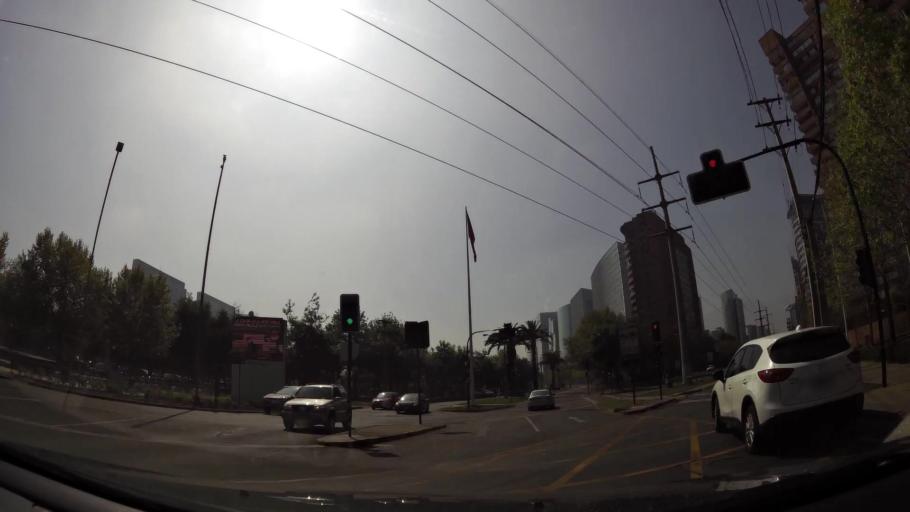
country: CL
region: Santiago Metropolitan
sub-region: Provincia de Santiago
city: Villa Presidente Frei, Nunoa, Santiago, Chile
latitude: -33.4057
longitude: -70.5793
